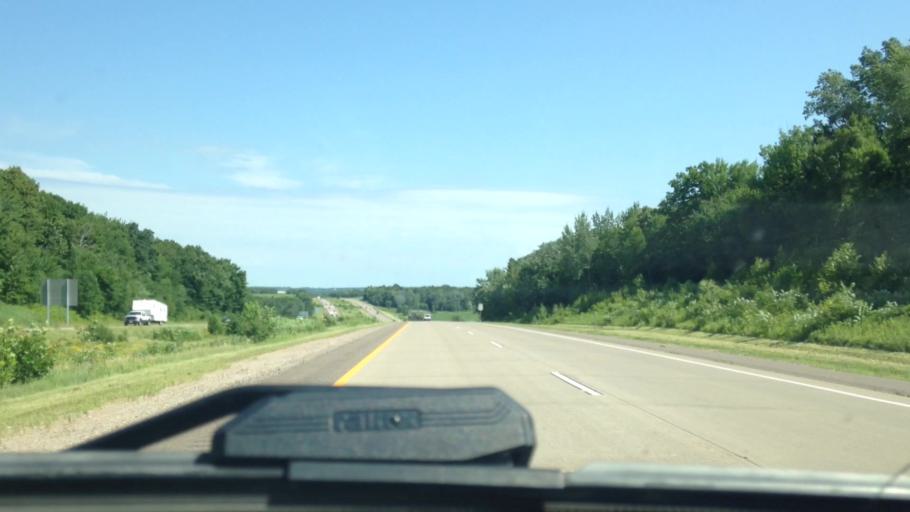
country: US
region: Wisconsin
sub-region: Barron County
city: Rice Lake
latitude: 45.5208
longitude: -91.7596
